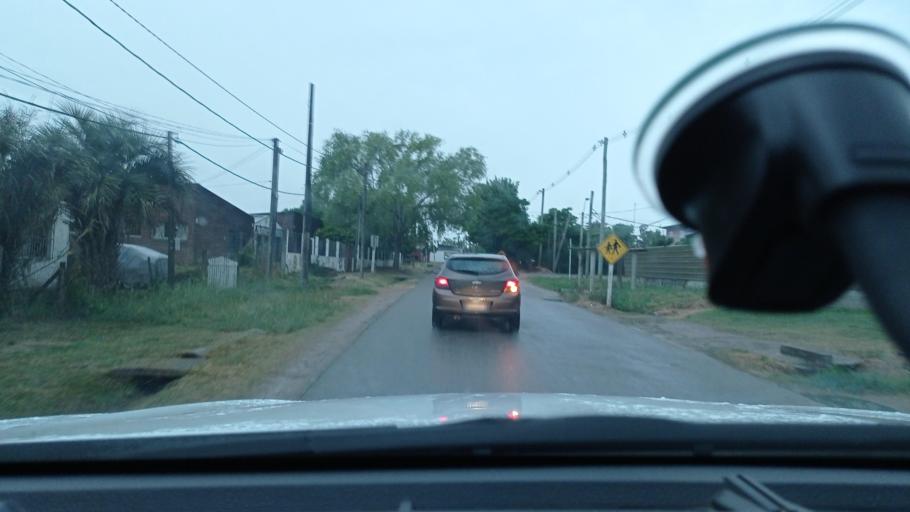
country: UY
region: Canelones
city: Joaquin Suarez
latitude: -34.7544
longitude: -56.0149
